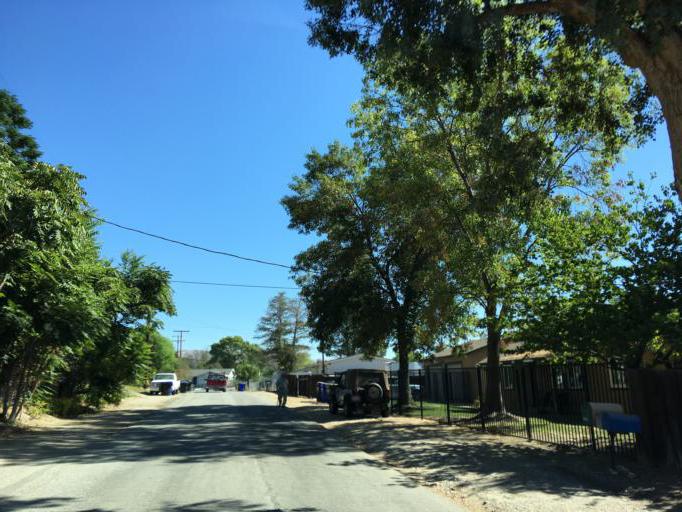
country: US
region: California
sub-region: Los Angeles County
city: Agua Dulce
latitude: 34.4454
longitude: -118.4289
